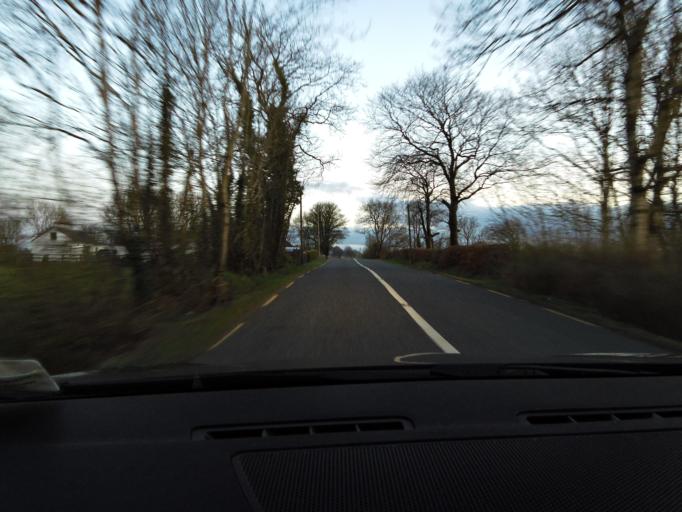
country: IE
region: Connaught
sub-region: Roscommon
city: Boyle
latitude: 53.8911
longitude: -8.2503
